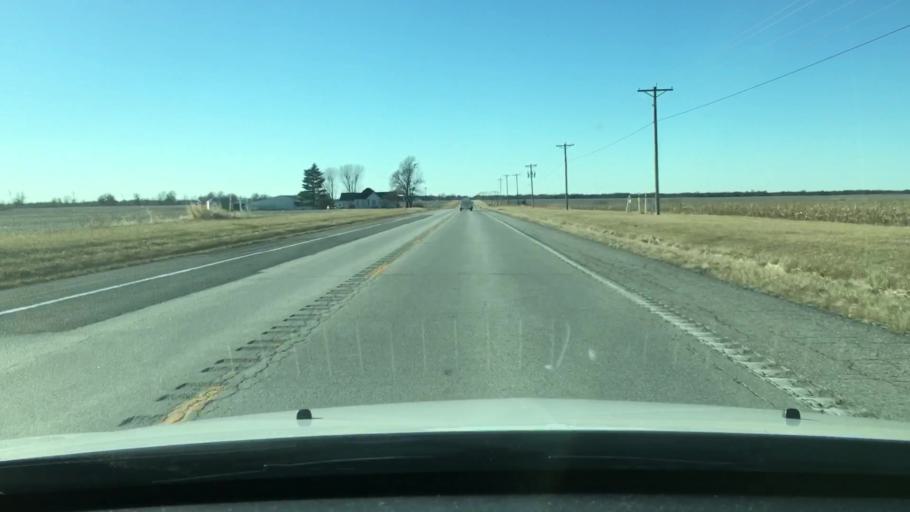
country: US
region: Missouri
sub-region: Audrain County
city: Vandalia
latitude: 39.3458
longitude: -91.3619
